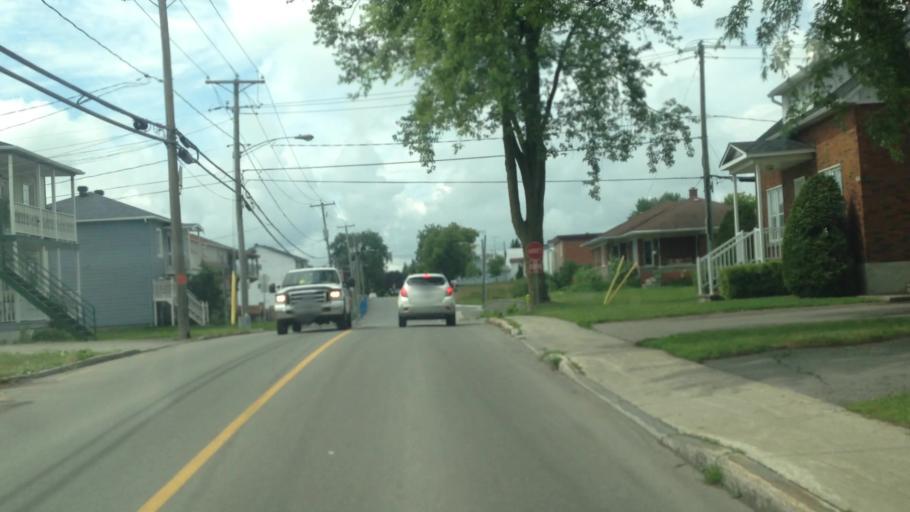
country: CA
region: Quebec
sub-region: Laurentides
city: Blainville
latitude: 45.7036
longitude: -73.9298
